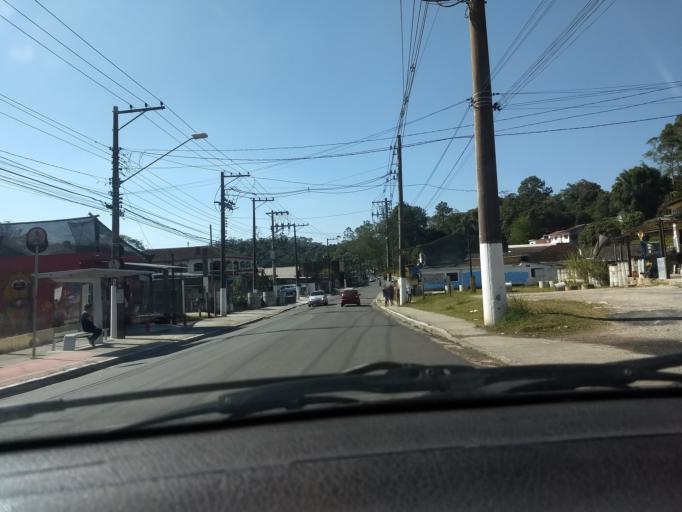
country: BR
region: Sao Paulo
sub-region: Embu-Guacu
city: Embu Guacu
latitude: -23.8383
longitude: -46.7329
